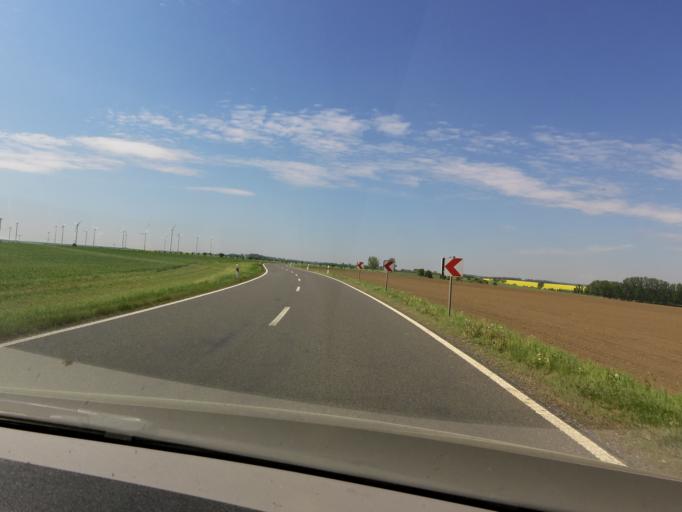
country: DE
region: Thuringia
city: Urleben
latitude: 51.1487
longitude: 10.7819
